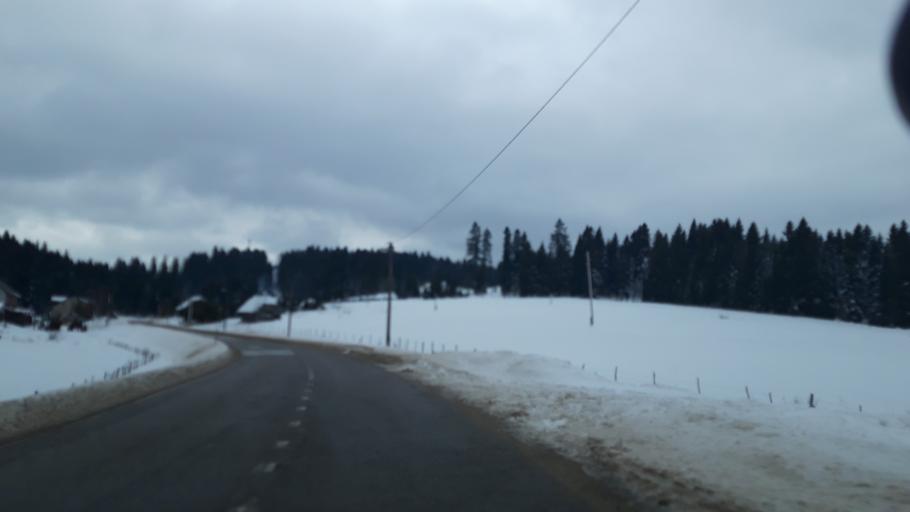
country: BA
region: Republika Srpska
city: Han Pijesak
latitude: 44.0929
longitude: 18.9555
